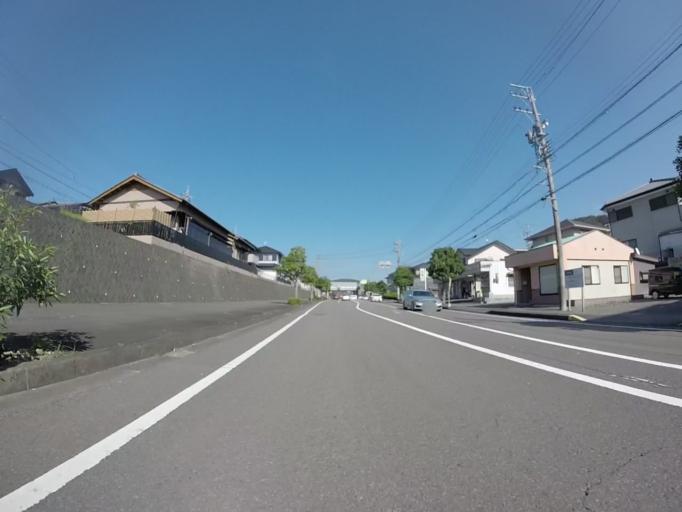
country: JP
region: Shizuoka
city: Fujieda
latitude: 34.8902
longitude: 138.2625
